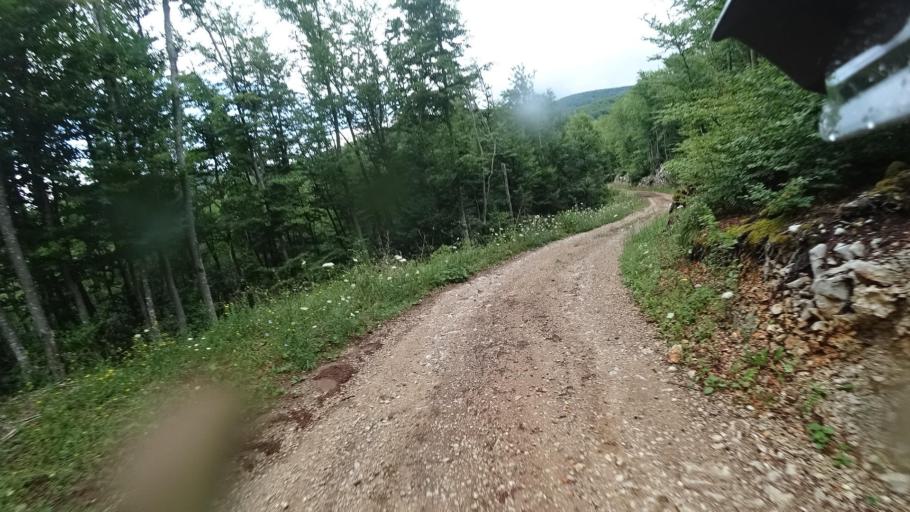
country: HR
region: Licko-Senjska
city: Jezerce
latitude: 44.7315
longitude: 15.6424
